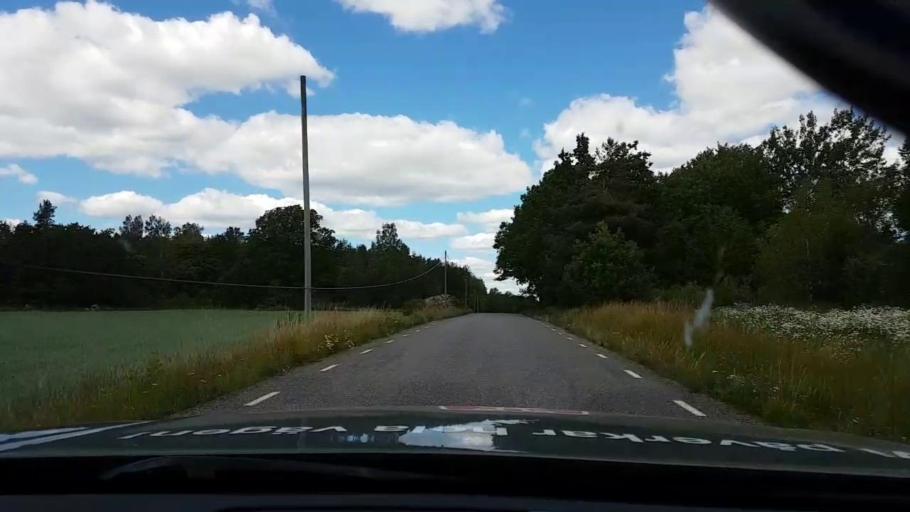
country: SE
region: Kalmar
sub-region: Vasterviks Kommun
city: Forserum
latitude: 57.9941
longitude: 16.6000
